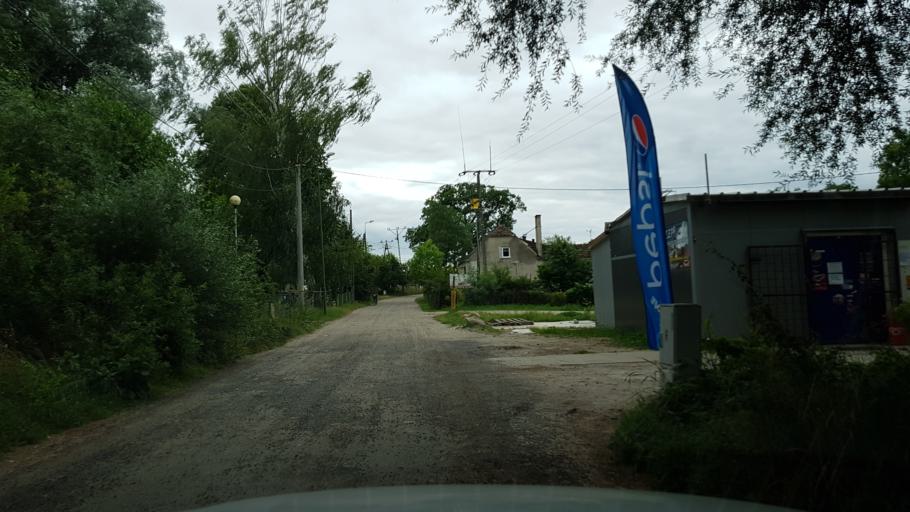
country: PL
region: West Pomeranian Voivodeship
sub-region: Powiat kamienski
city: Dziwnow
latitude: 53.9908
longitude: 14.6859
